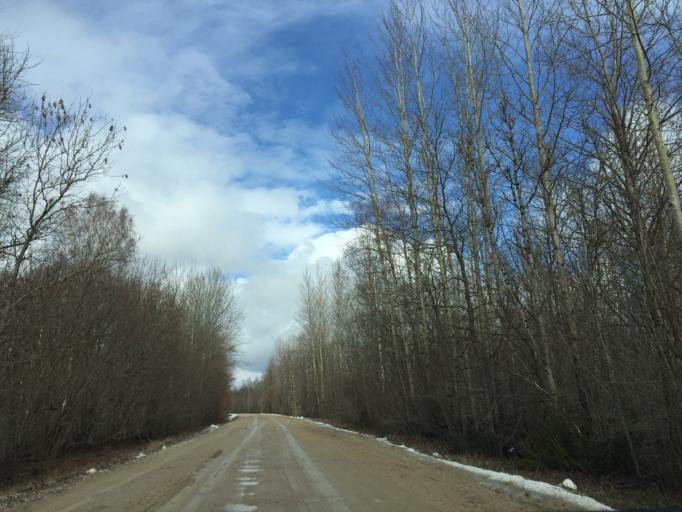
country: EE
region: Laeaene
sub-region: Lihula vald
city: Lihula
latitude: 58.7235
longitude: 23.8298
